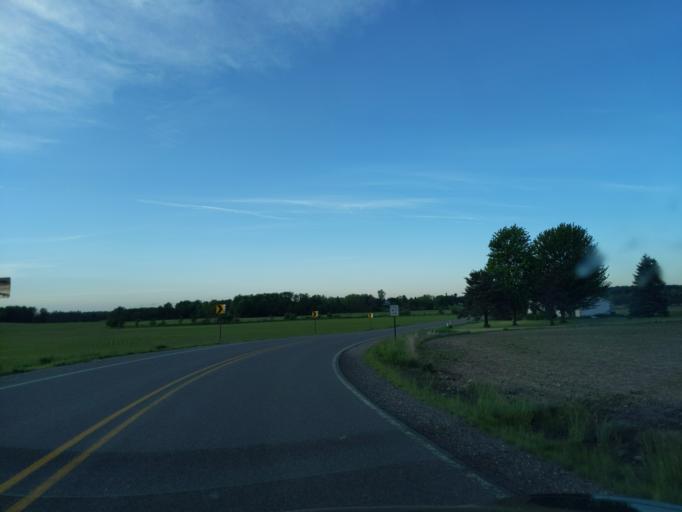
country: US
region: Michigan
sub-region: Ingham County
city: Williamston
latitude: 42.5610
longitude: -84.3031
